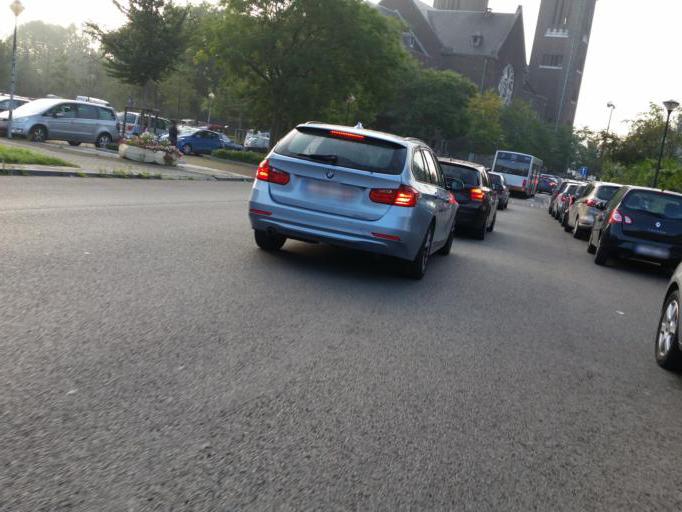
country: BE
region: Flanders
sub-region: Provincie Vlaams-Brabant
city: Grimbergen
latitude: 50.8968
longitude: 4.3869
